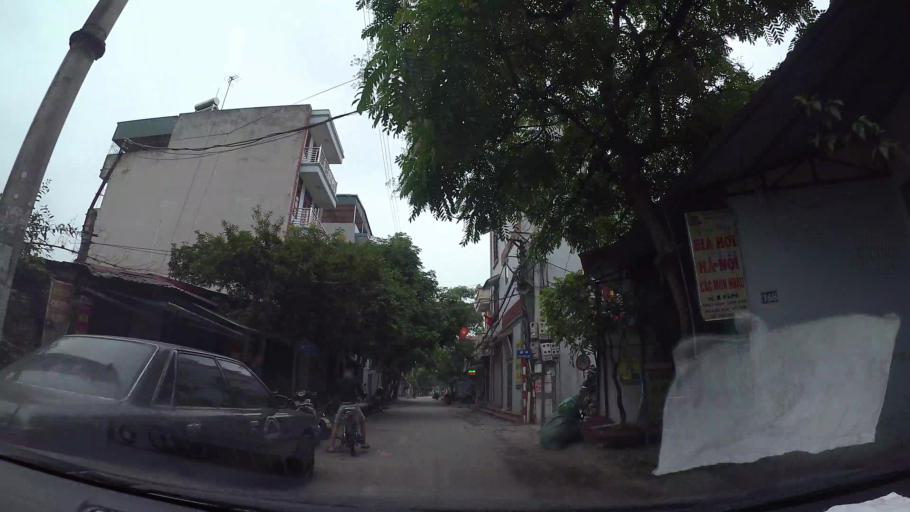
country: VN
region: Hung Yen
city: Van Giang
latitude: 20.9719
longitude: 105.8939
